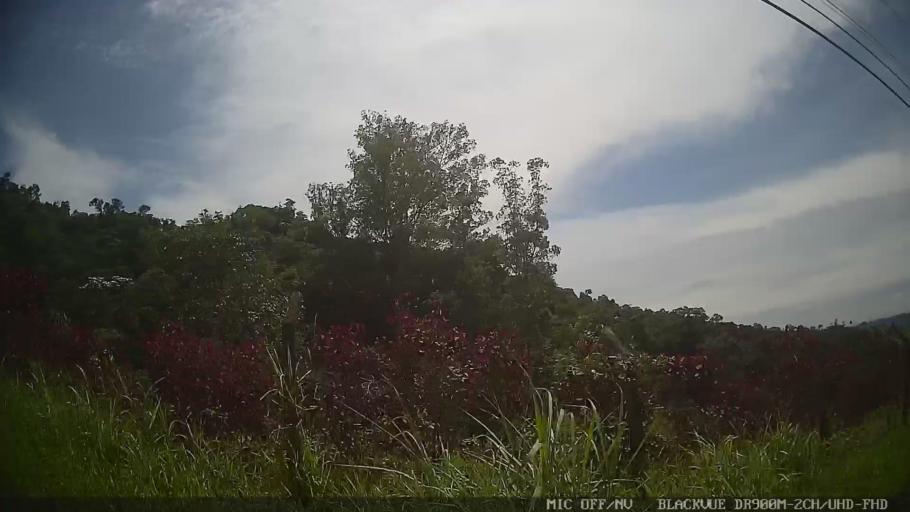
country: BR
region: Sao Paulo
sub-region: Santa Isabel
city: Santa Isabel
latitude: -23.3482
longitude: -46.2013
